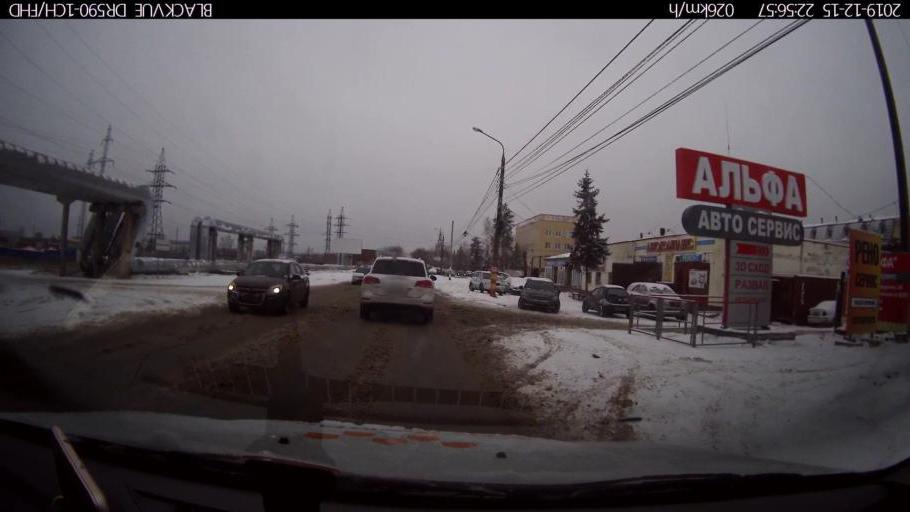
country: RU
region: Nizjnij Novgorod
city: Neklyudovo
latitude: 56.3471
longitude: 43.8916
